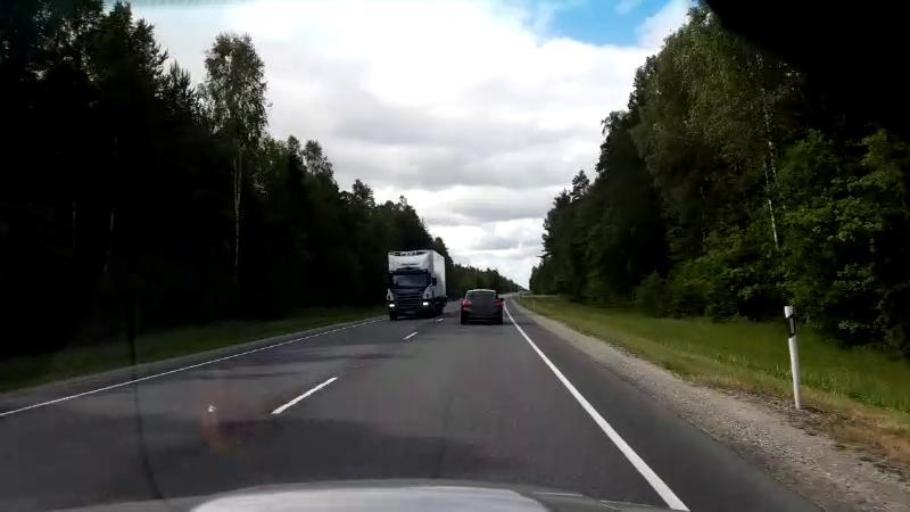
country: EE
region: Raplamaa
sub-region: Maerjamaa vald
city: Marjamaa
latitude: 58.8863
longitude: 24.4520
